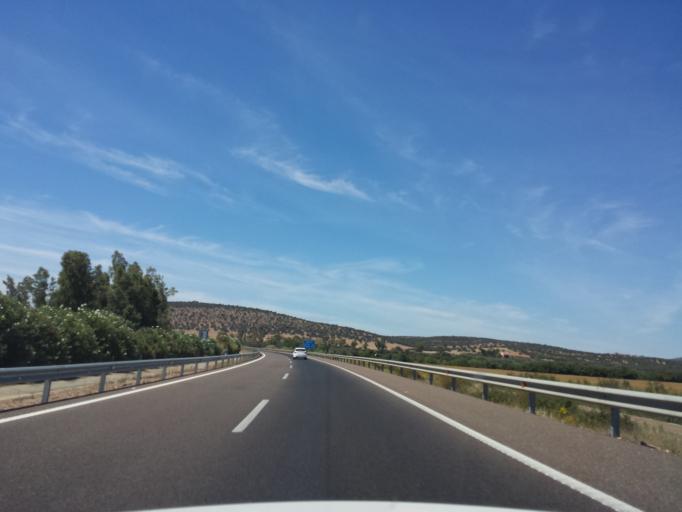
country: ES
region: Extremadura
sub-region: Provincia de Badajoz
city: San Pedro de Merida
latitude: 38.9888
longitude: -6.1312
